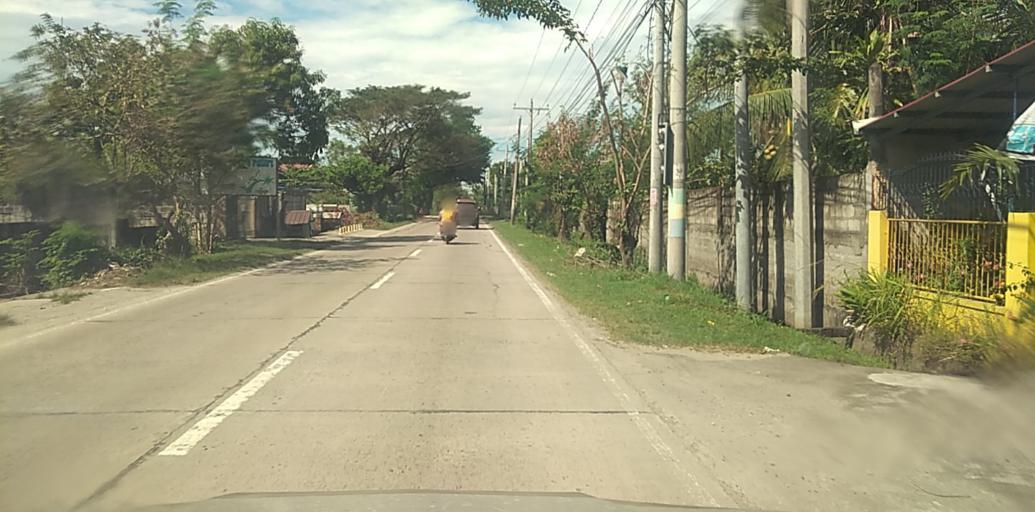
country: PH
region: Central Luzon
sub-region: Province of Pampanga
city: Arayat
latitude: 15.1529
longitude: 120.7345
